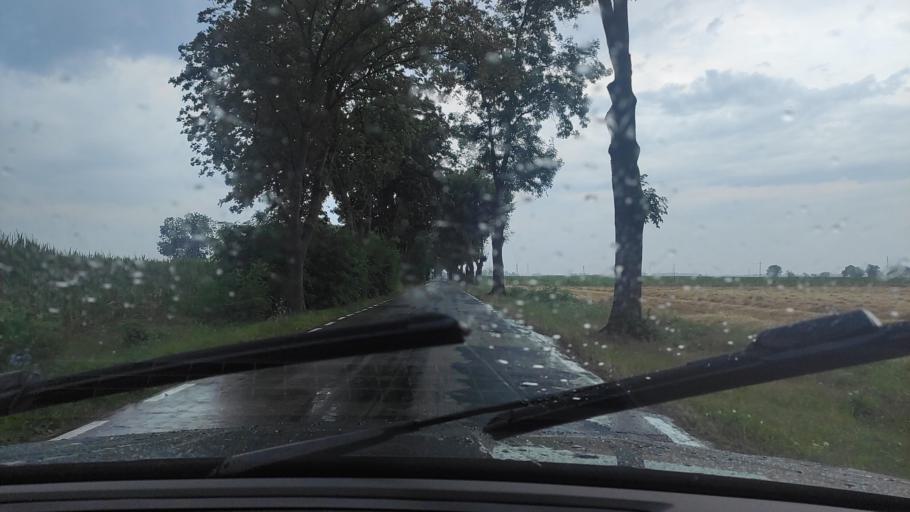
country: PL
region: Greater Poland Voivodeship
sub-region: Powiat poznanski
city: Kleszczewo
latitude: 52.2896
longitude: 17.1878
